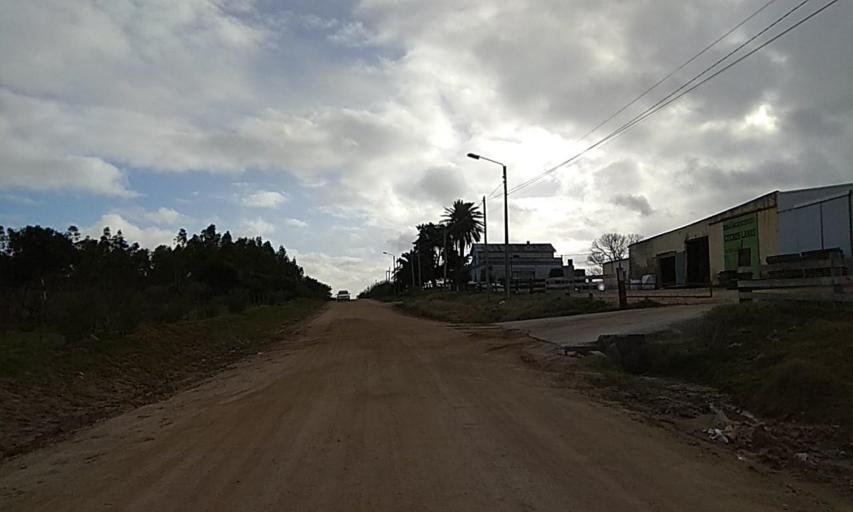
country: UY
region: Florida
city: Florida
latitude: -34.0688
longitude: -56.1947
